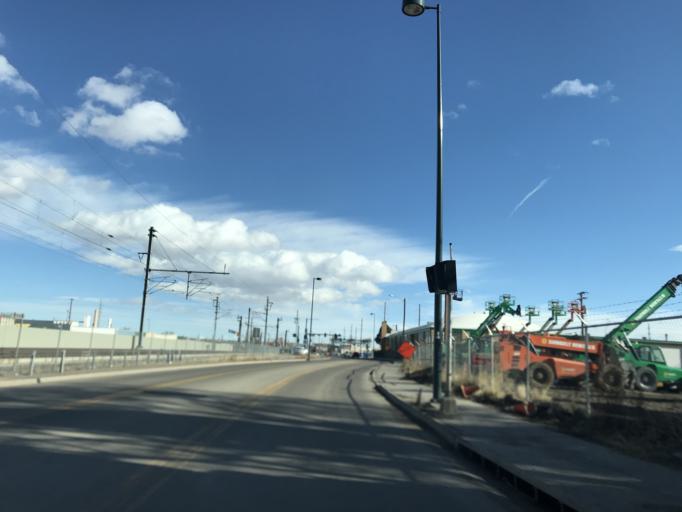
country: US
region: Colorado
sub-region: Denver County
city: Denver
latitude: 39.7727
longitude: -104.9619
